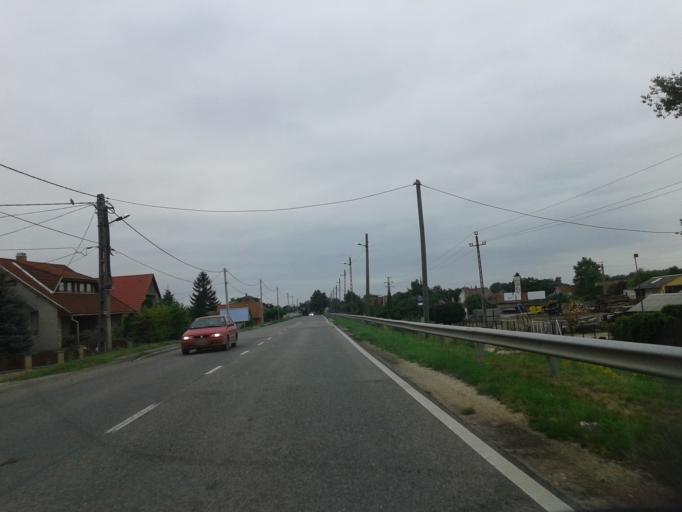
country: HU
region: Pest
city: Domsod
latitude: 47.1007
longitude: 19.0121
